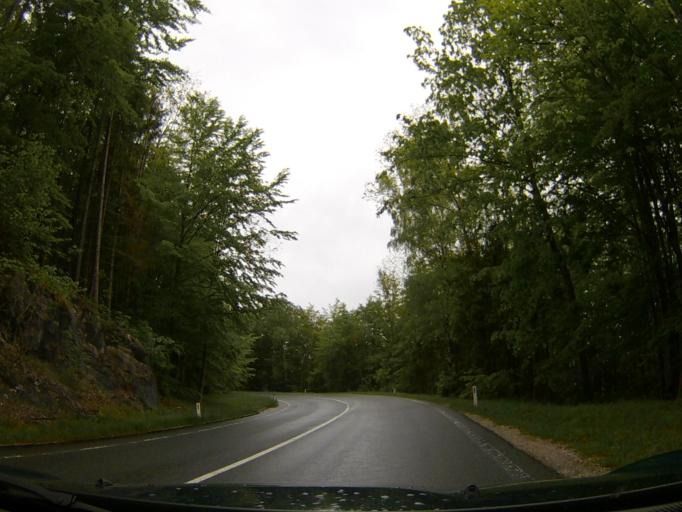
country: AT
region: Salzburg
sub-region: Politischer Bezirk Salzburg-Umgebung
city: Sankt Gilgen
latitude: 47.7916
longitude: 13.3935
